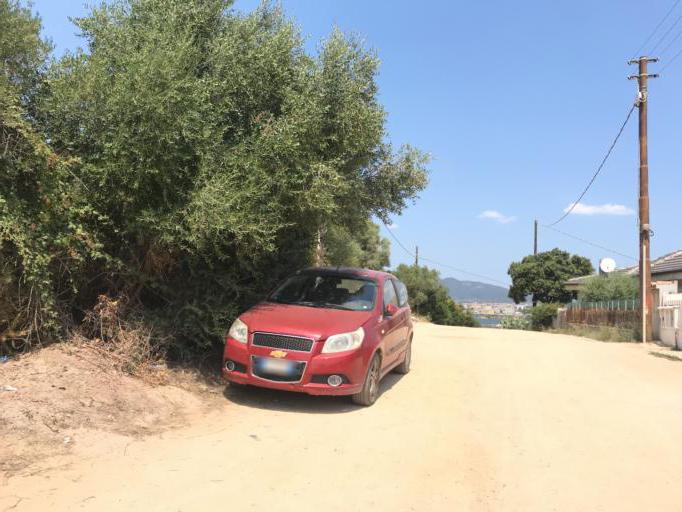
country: IT
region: Sardinia
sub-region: Provincia di Olbia-Tempio
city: Olbia
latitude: 40.9119
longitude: 9.5149
